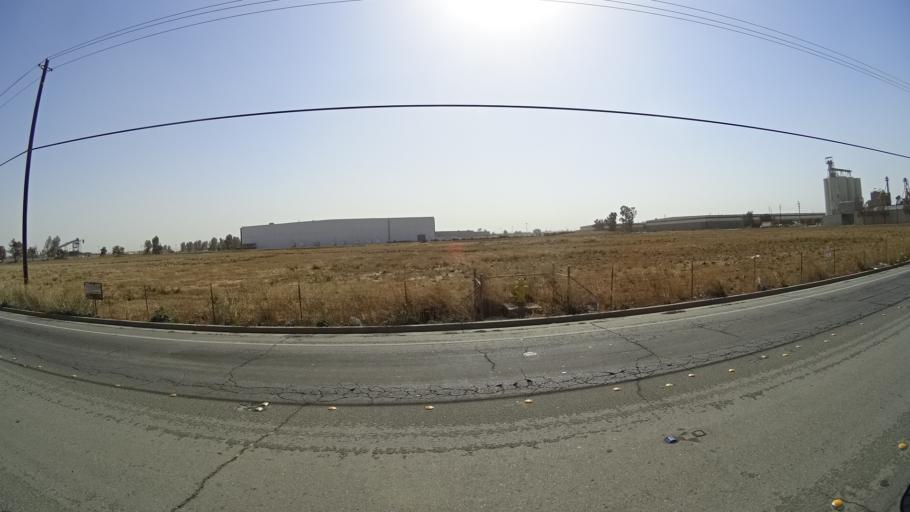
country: US
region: California
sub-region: Yolo County
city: Woodland
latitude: 38.6919
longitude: -121.7408
